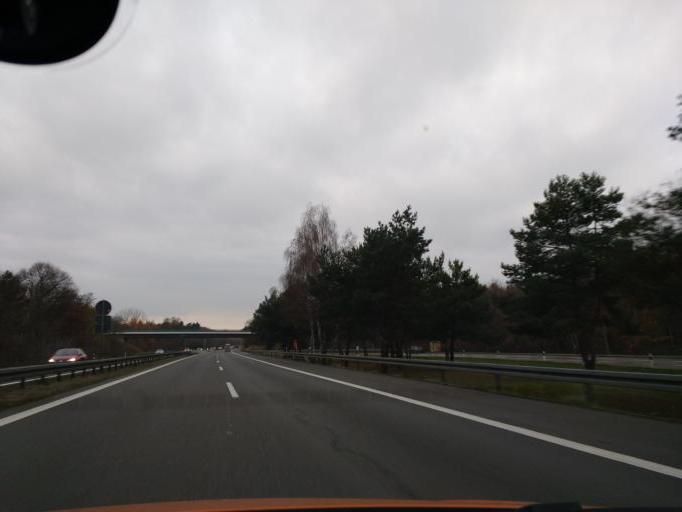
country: DE
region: Brandenburg
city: Fehrbellin
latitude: 52.7661
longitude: 12.8215
